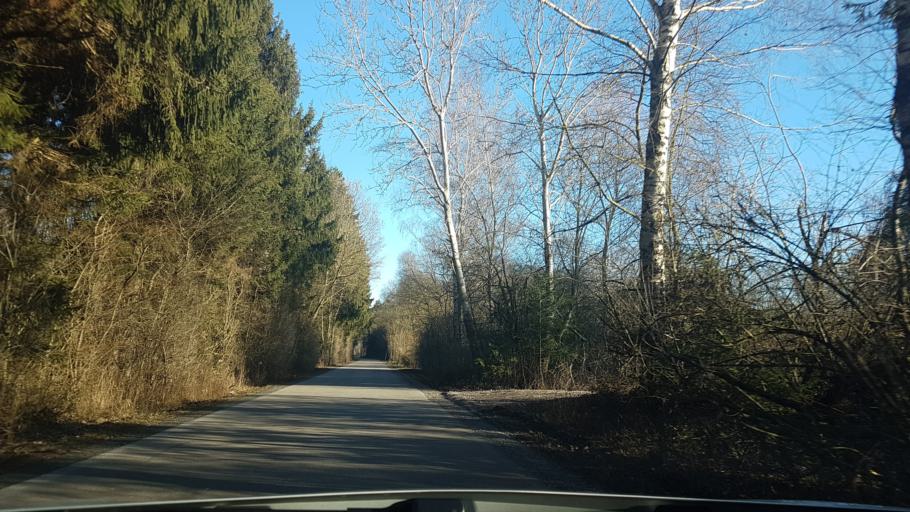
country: DE
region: Bavaria
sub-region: Upper Bavaria
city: Eichenried
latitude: 48.2812
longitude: 11.7603
